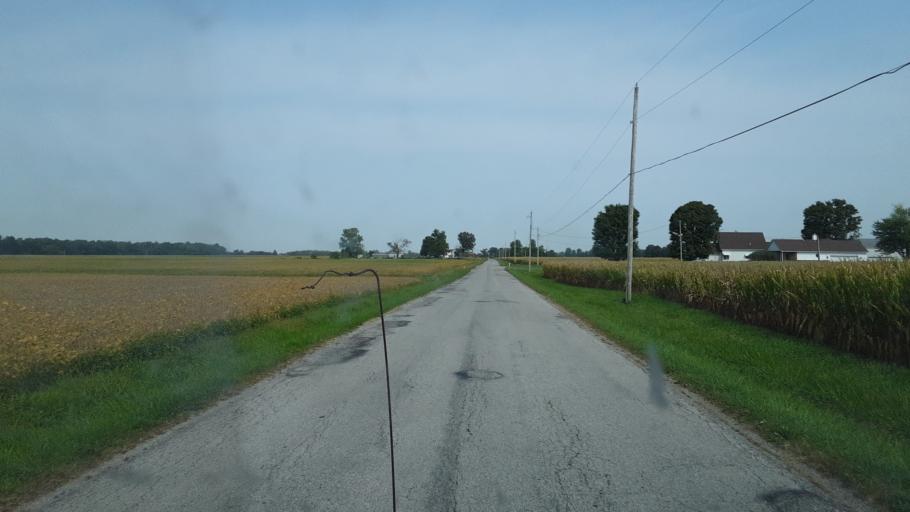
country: US
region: Ohio
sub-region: Morrow County
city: Cardington
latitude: 40.5945
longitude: -82.9186
